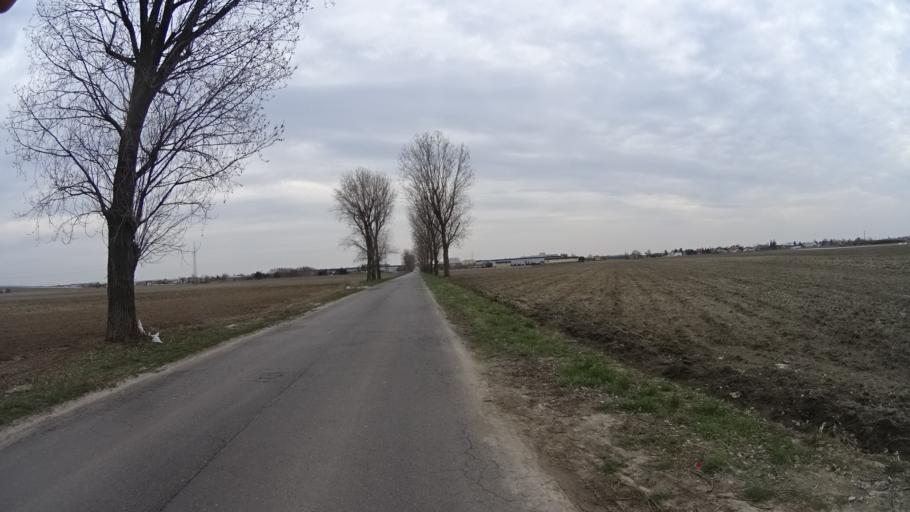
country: PL
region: Masovian Voivodeship
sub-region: Powiat warszawski zachodni
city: Ozarow Mazowiecki
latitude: 52.2048
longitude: 20.8214
